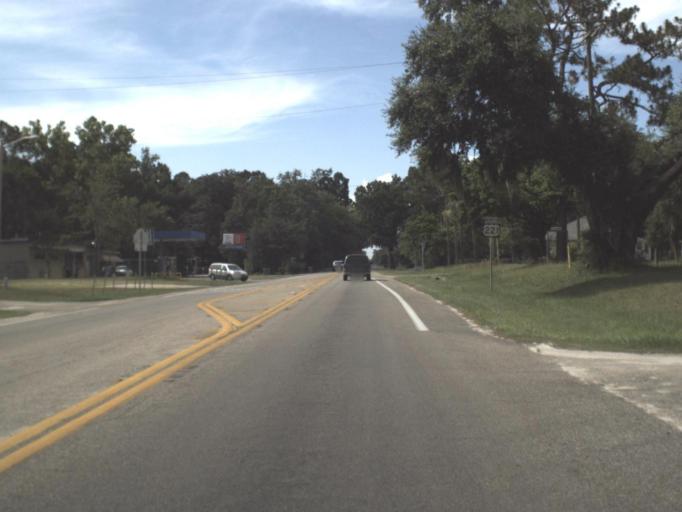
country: US
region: Florida
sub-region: Taylor County
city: Perry
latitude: 30.1289
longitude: -83.5827
